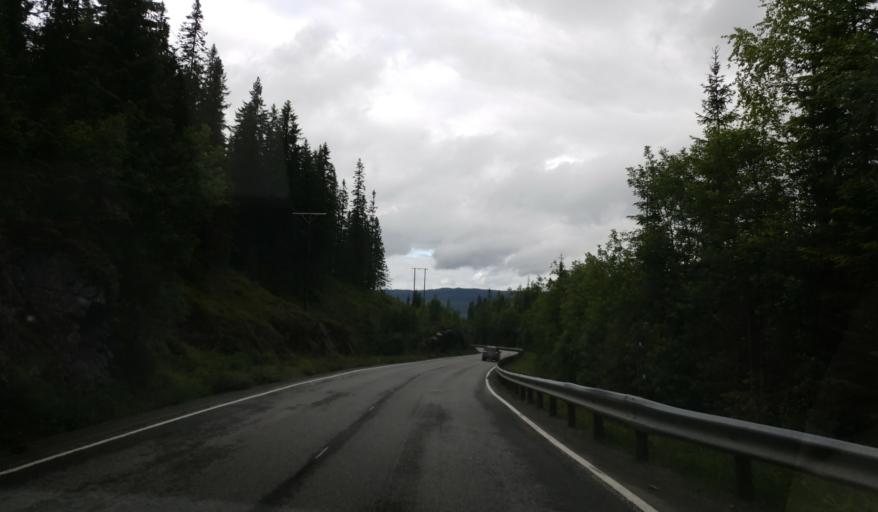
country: NO
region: Sor-Trondelag
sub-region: Selbu
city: Mebonden
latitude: 63.3603
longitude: 11.0779
